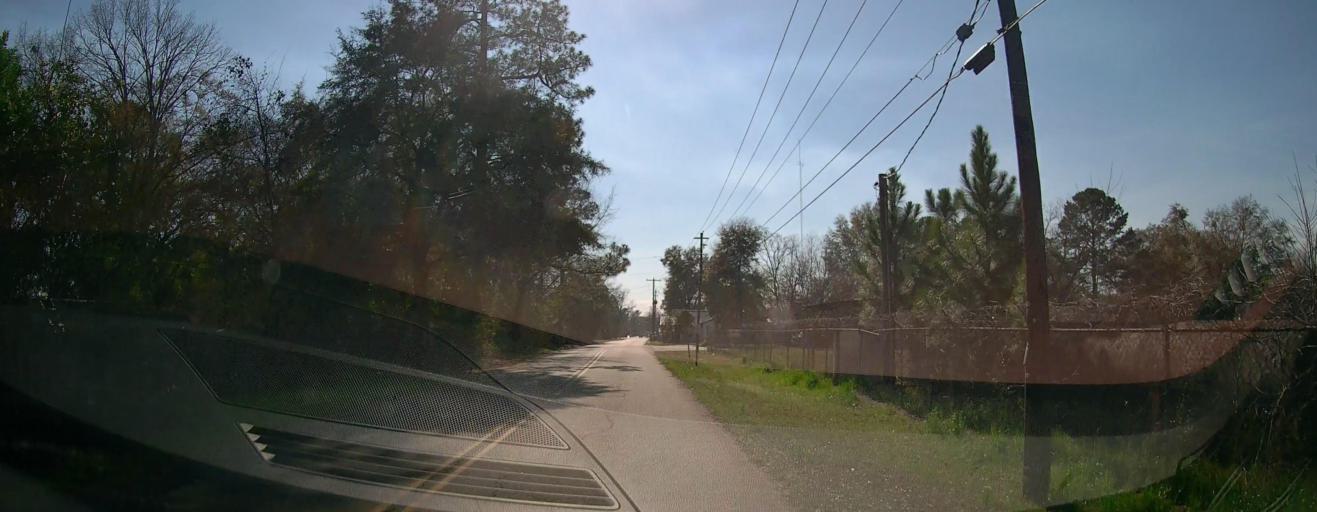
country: US
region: Georgia
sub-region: Macon County
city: Montezuma
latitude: 32.2892
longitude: -84.0105
